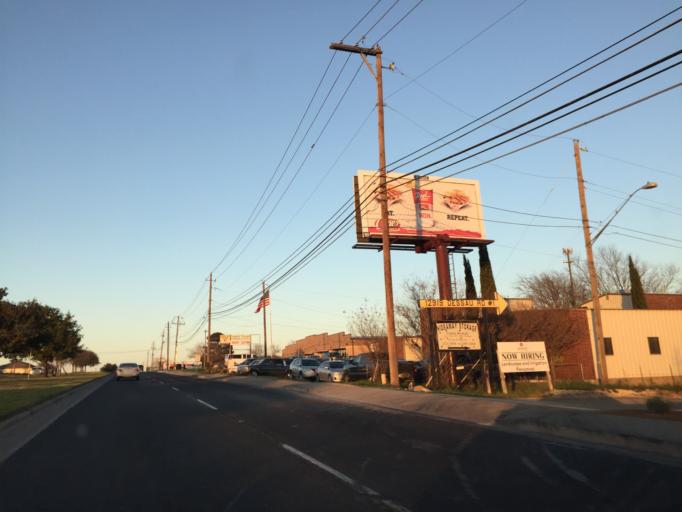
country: US
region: Texas
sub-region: Travis County
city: Pflugerville
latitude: 30.3979
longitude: -97.6421
